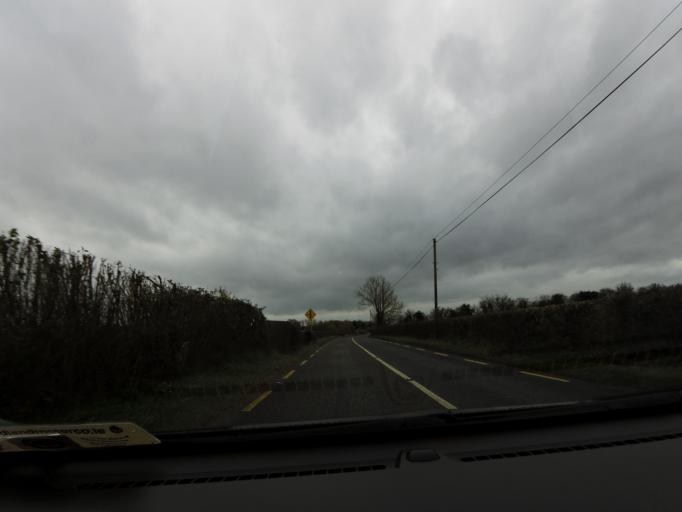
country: IE
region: Leinster
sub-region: Kilkenny
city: Ballyragget
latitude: 52.7577
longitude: -7.3294
